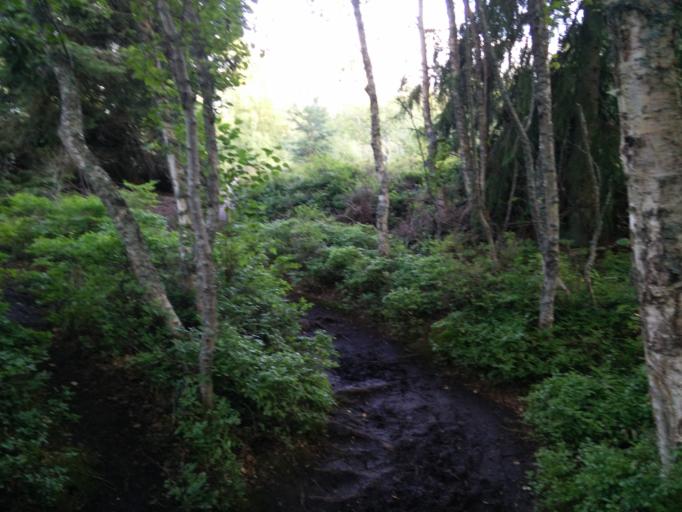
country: SE
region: Stockholm
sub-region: Norrtalje Kommun
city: Bjorko
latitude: 59.5952
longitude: 19.1634
